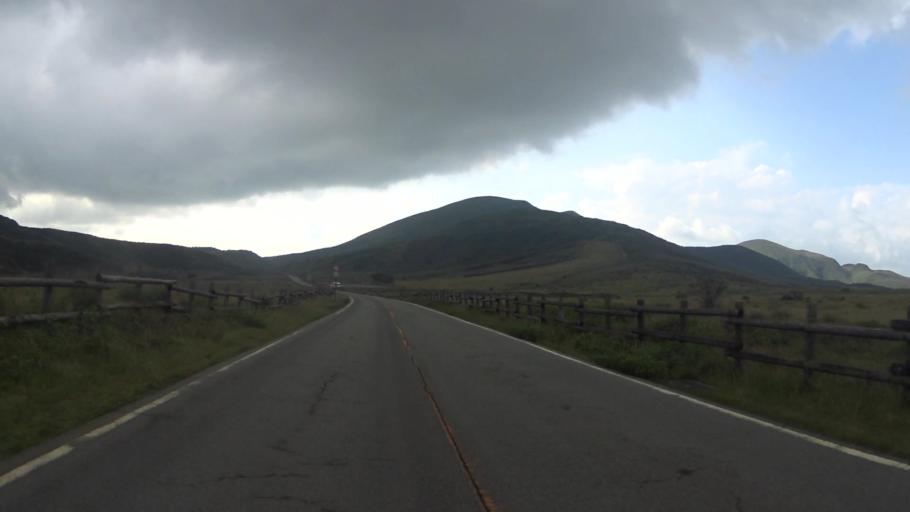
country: JP
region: Kumamoto
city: Aso
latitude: 32.8823
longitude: 131.0683
